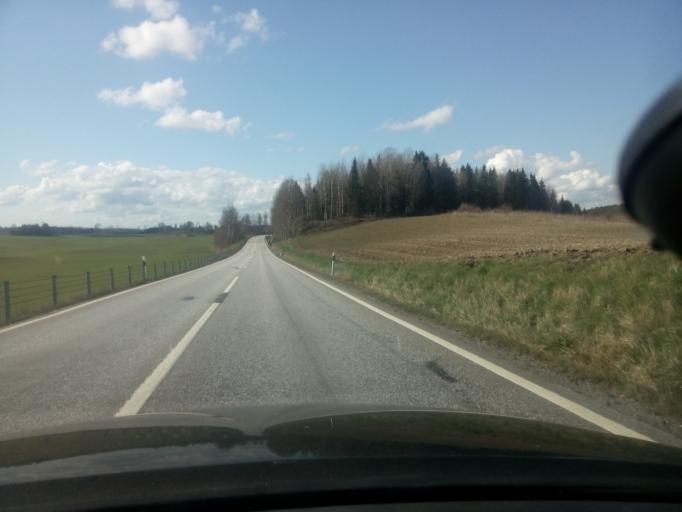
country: SE
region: Soedermanland
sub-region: Flens Kommun
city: Malmkoping
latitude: 59.1053
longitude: 16.7735
